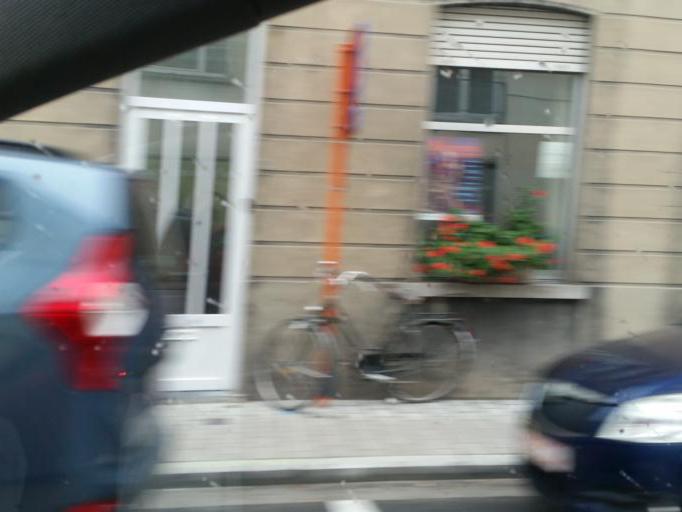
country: BE
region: Flanders
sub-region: Provincie Oost-Vlaanderen
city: Ledeberg
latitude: 51.0434
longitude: 3.7582
